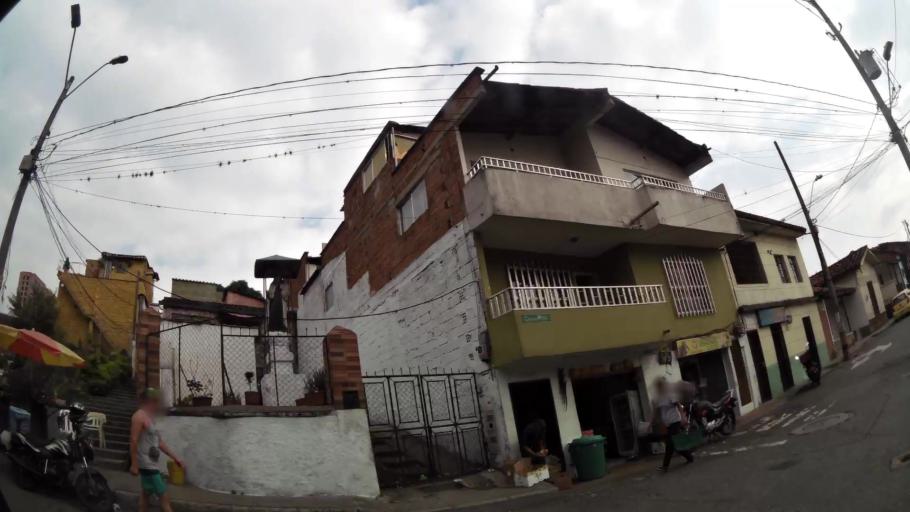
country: CO
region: Antioquia
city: Medellin
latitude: 6.2782
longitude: -75.5942
